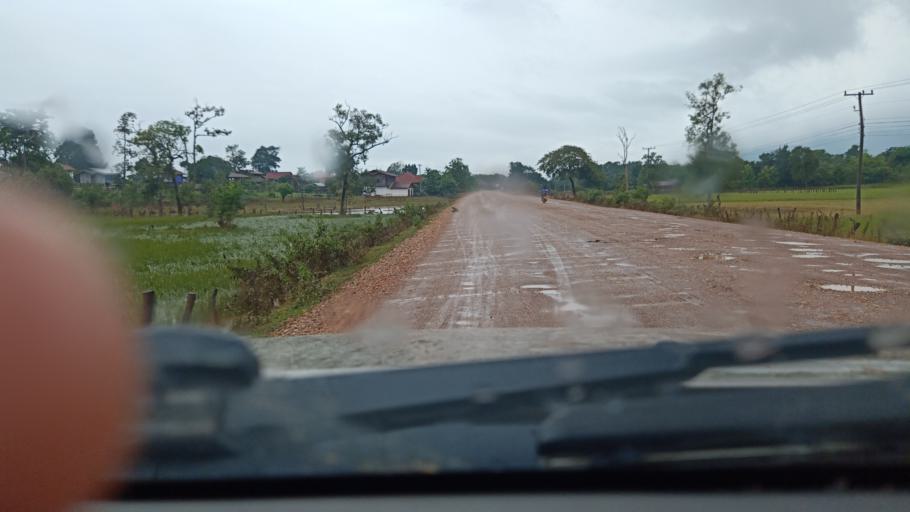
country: LA
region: Attapu
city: Attapu
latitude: 14.7135
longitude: 106.6646
